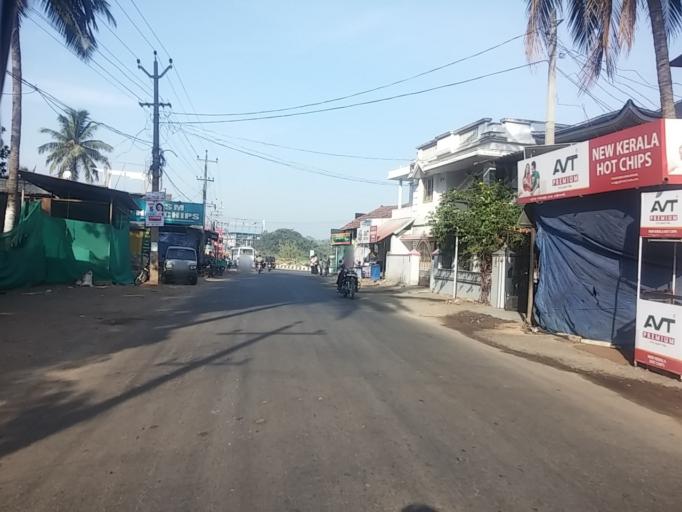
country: IN
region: Kerala
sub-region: Thrissur District
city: Chelakara
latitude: 10.6006
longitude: 76.4914
